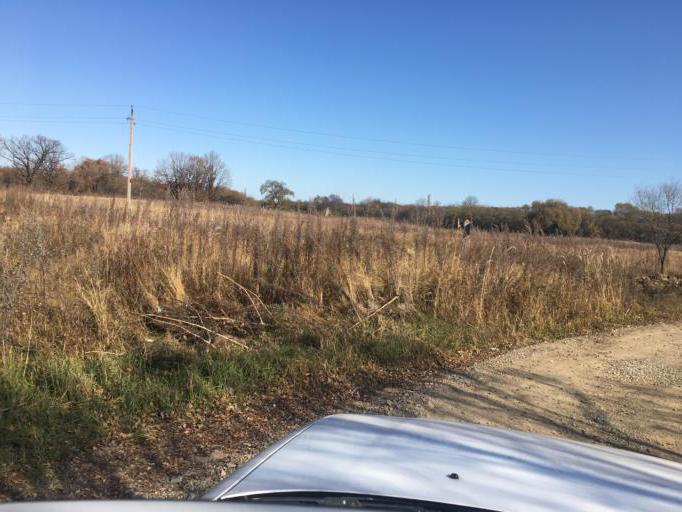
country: RU
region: Primorskiy
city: Dal'nerechensk
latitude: 45.9185
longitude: 133.7883
